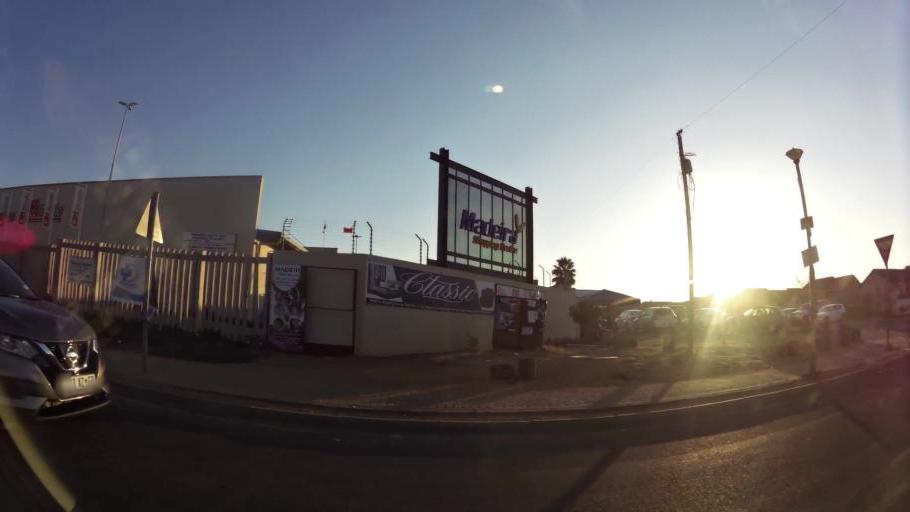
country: ZA
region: Gauteng
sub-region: City of Tshwane Metropolitan Municipality
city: Pretoria
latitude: -25.7465
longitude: 28.1145
